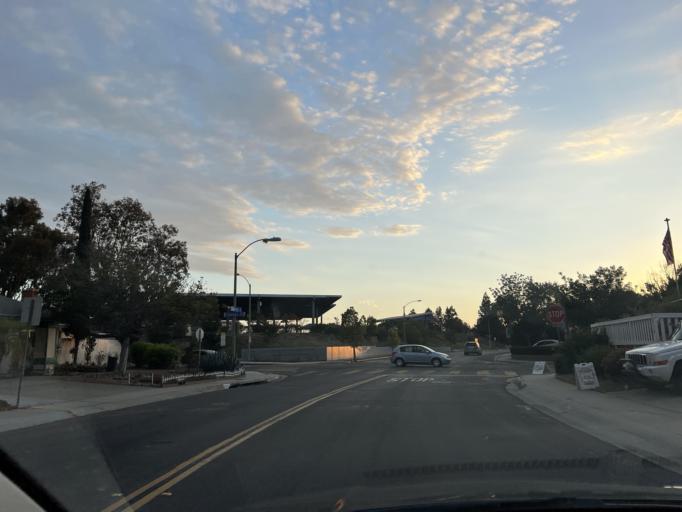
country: US
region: California
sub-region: San Diego County
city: Fairbanks Ranch
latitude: 32.9068
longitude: -117.1540
